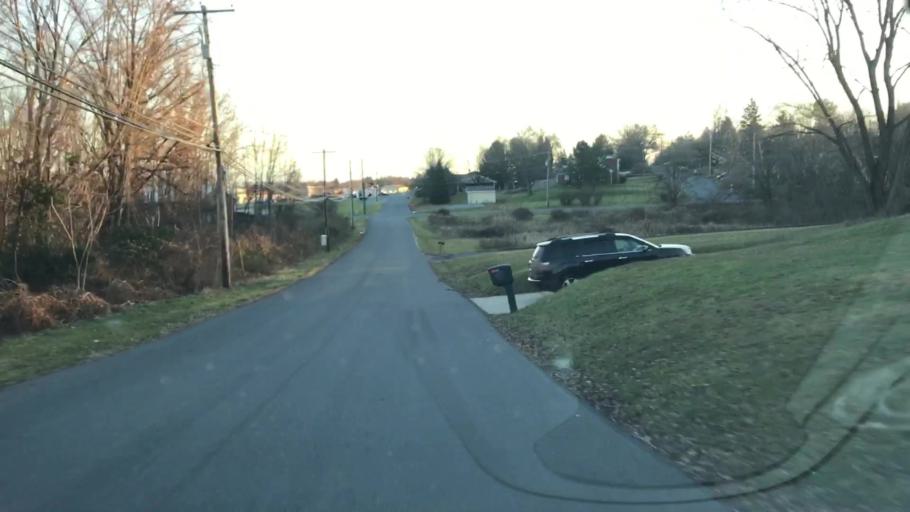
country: US
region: Pennsylvania
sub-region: Dauphin County
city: Skyline View
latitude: 40.3342
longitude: -76.7284
